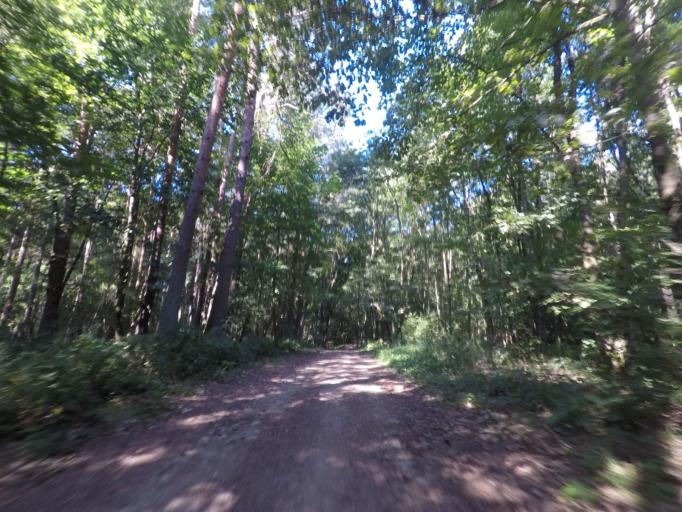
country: LU
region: Luxembourg
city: Itzig
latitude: 49.6090
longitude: 6.1775
